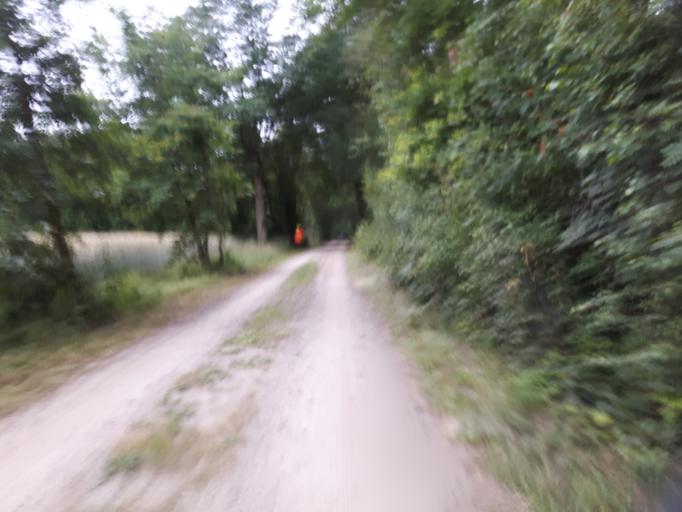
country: DE
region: Lower Saxony
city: Garstedt
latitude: 53.3131
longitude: 10.1961
